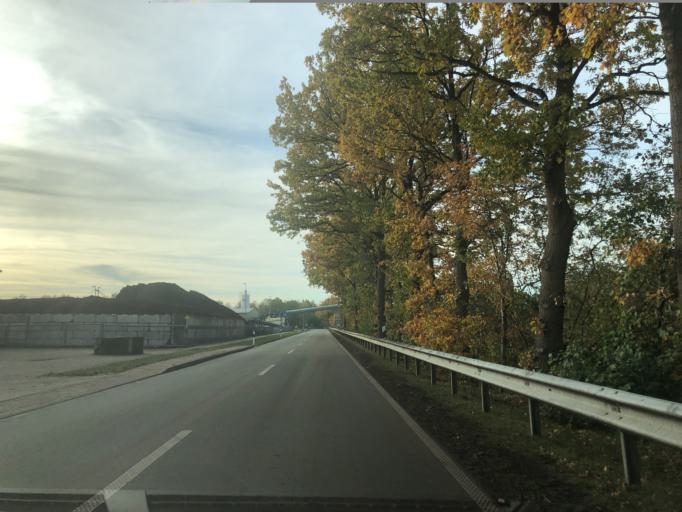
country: DE
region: Lower Saxony
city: Edewecht
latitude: 53.0848
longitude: 7.9624
